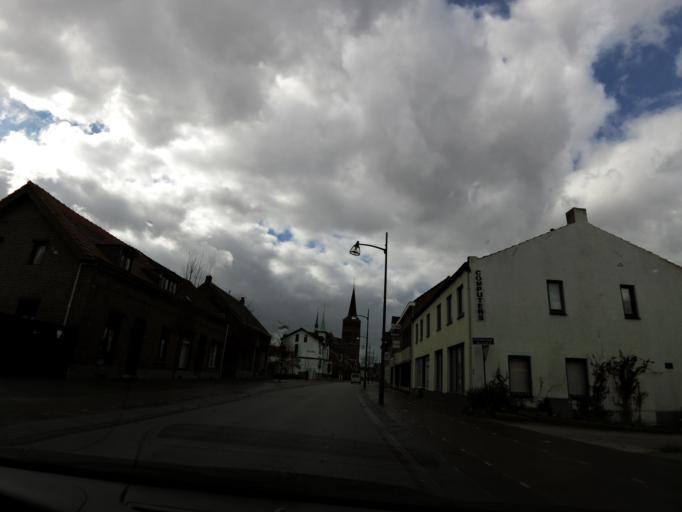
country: NL
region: Limburg
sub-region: Gemeente Venlo
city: Tegelen
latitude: 51.3450
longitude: 6.1396
